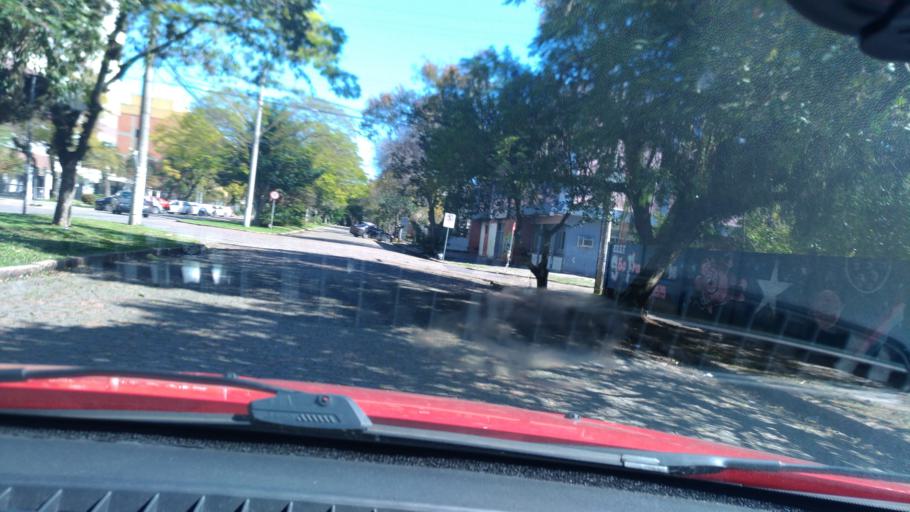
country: BR
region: Rio Grande do Sul
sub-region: Porto Alegre
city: Porto Alegre
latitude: -30.0447
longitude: -51.2021
